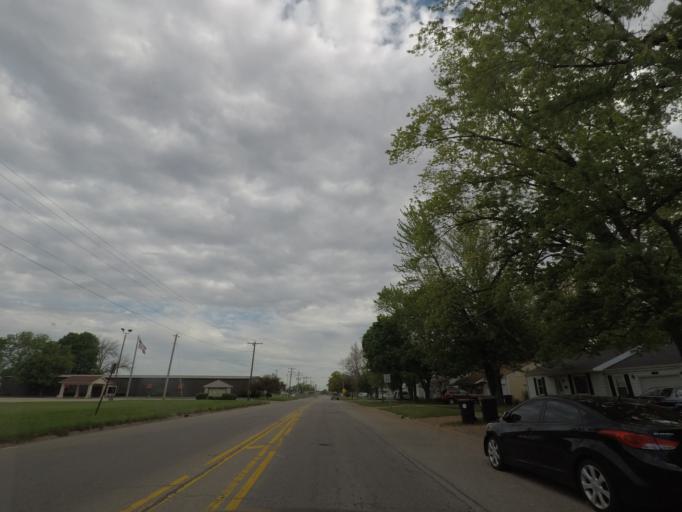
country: US
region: Illinois
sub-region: Logan County
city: Lincoln
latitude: 40.1389
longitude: -89.3488
